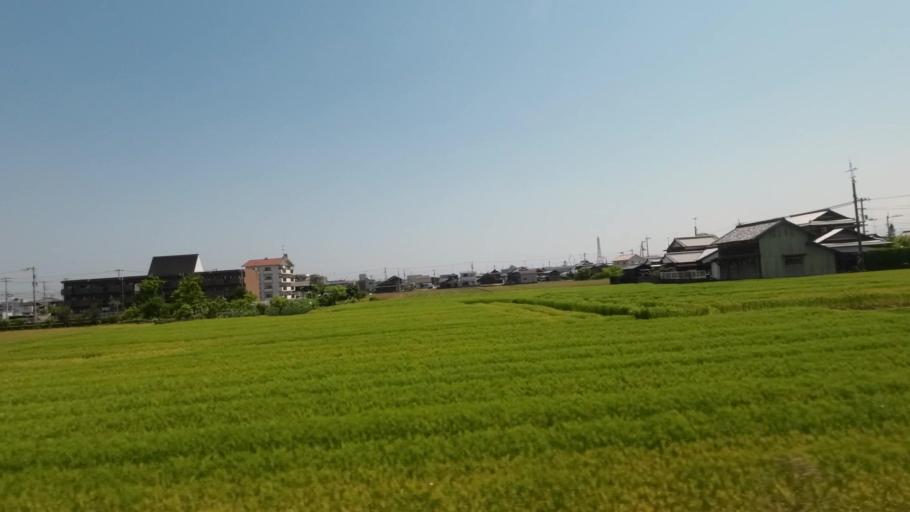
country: JP
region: Ehime
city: Saijo
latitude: 33.9266
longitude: 133.0883
